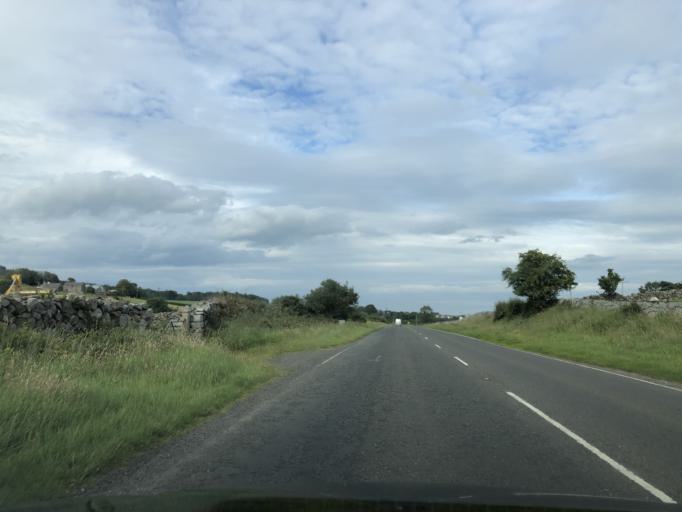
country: GB
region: Northern Ireland
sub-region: Down District
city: Castlewellan
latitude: 54.2466
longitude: -5.9759
